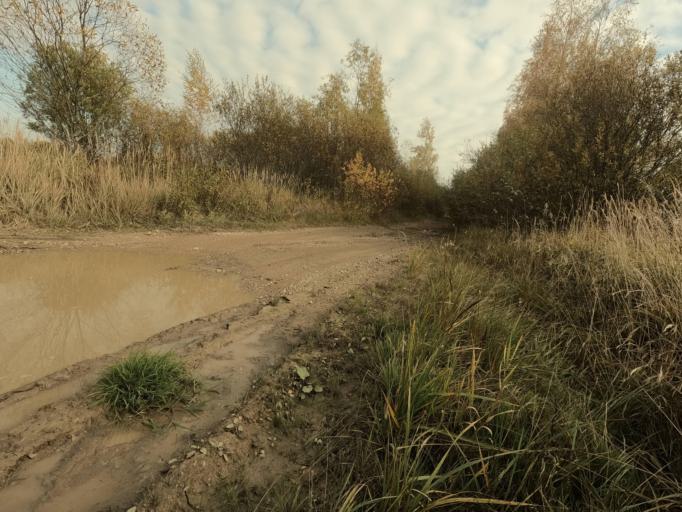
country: RU
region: Novgorod
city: Pankovka
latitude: 58.8797
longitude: 30.8056
